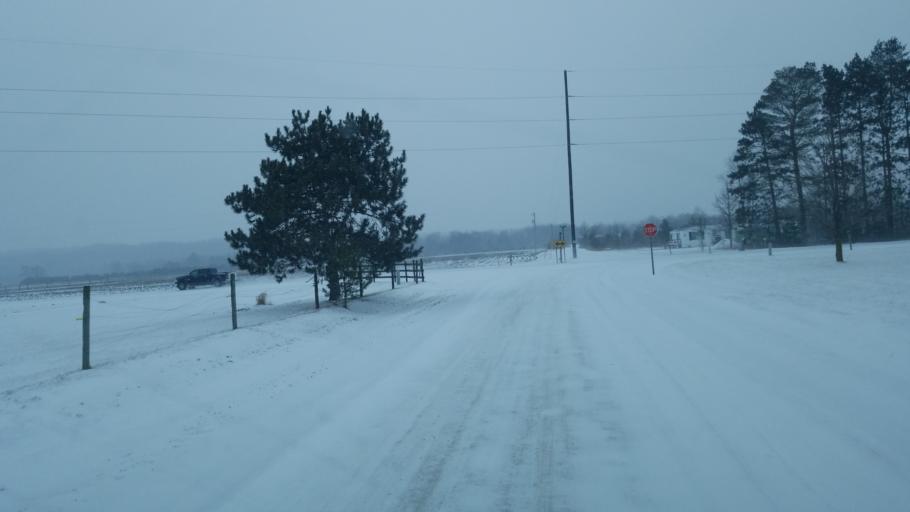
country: US
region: Michigan
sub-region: Osceola County
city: Reed City
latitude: 43.8292
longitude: -85.4233
